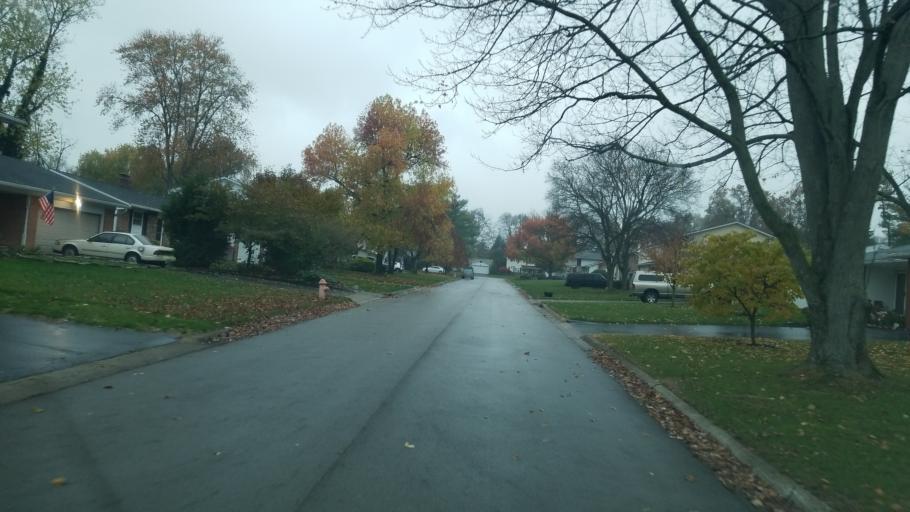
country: US
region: Ohio
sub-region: Franklin County
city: Upper Arlington
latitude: 40.0362
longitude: -83.0434
